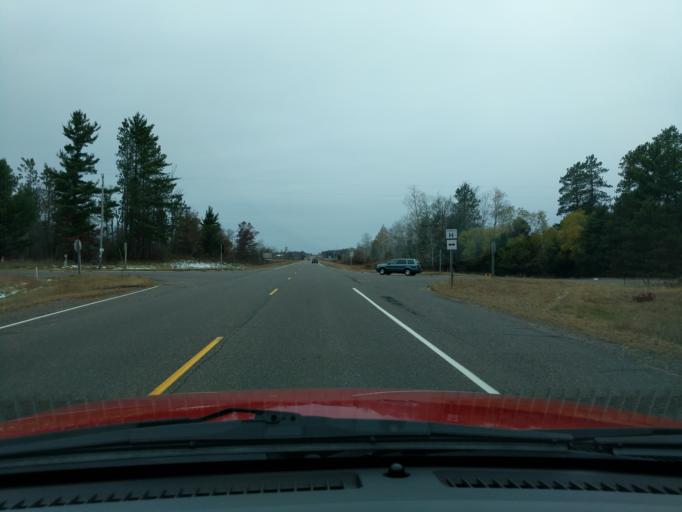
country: US
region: Wisconsin
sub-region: Washburn County
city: Shell Lake
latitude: 45.8155
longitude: -92.0925
